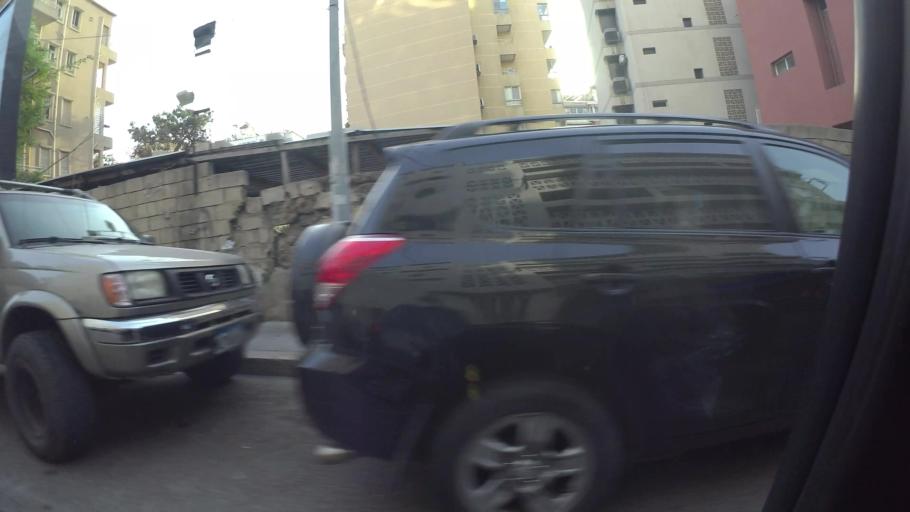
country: LB
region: Beyrouth
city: Ra's Bayrut
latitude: 33.8970
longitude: 35.4911
